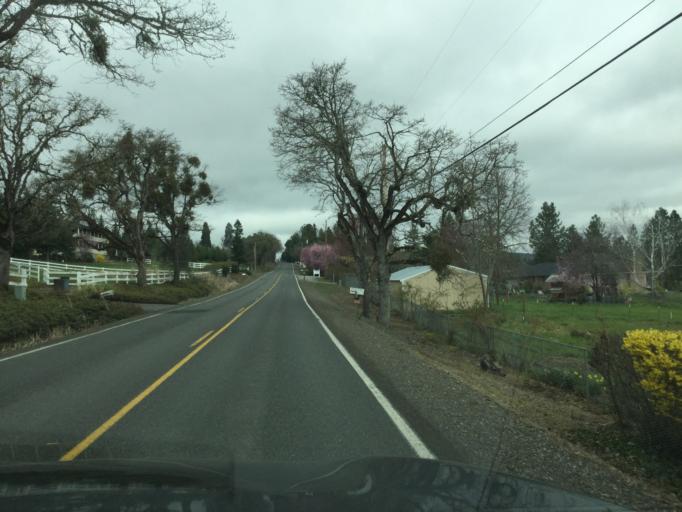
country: US
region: Oregon
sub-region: Jackson County
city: Central Point
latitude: 42.3807
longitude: -122.9636
